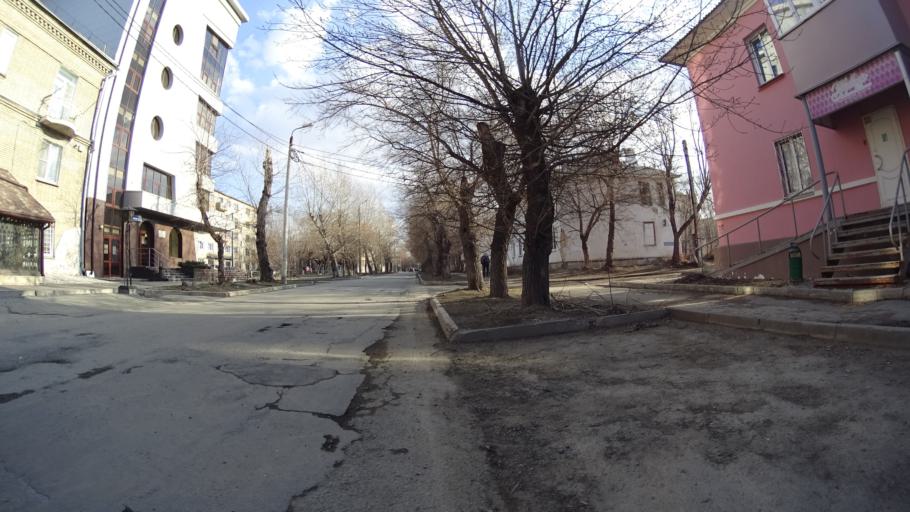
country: RU
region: Chelyabinsk
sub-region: Gorod Chelyabinsk
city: Chelyabinsk
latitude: 55.1472
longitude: 61.3746
